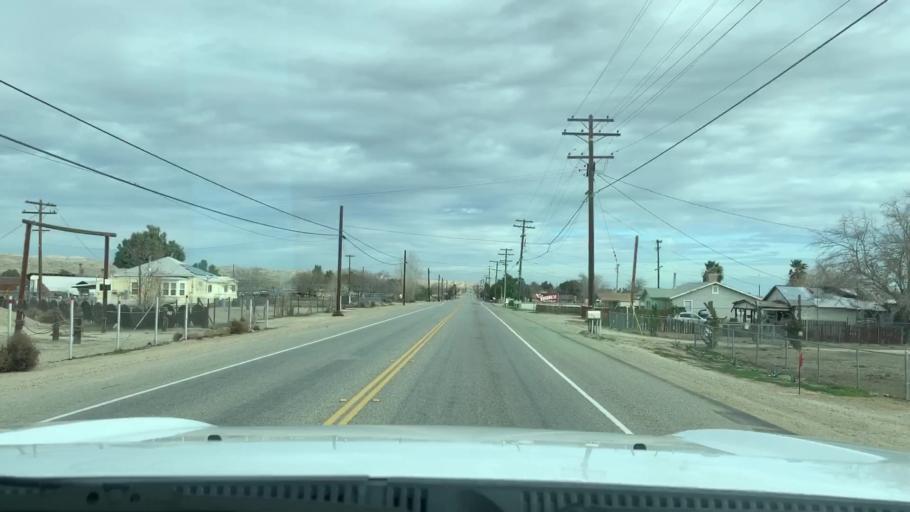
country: US
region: California
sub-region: Kern County
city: Ford City
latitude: 35.2188
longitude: -119.3915
